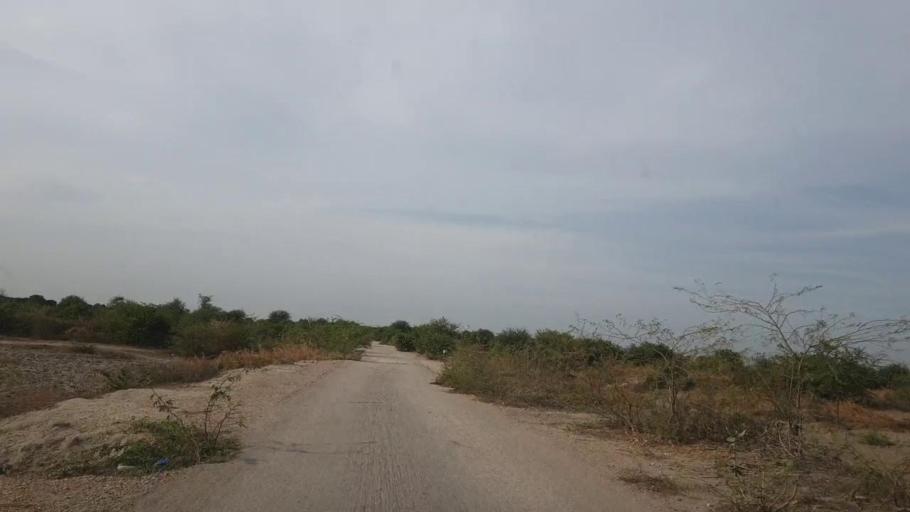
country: PK
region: Sindh
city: Nabisar
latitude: 24.9827
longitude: 69.5686
